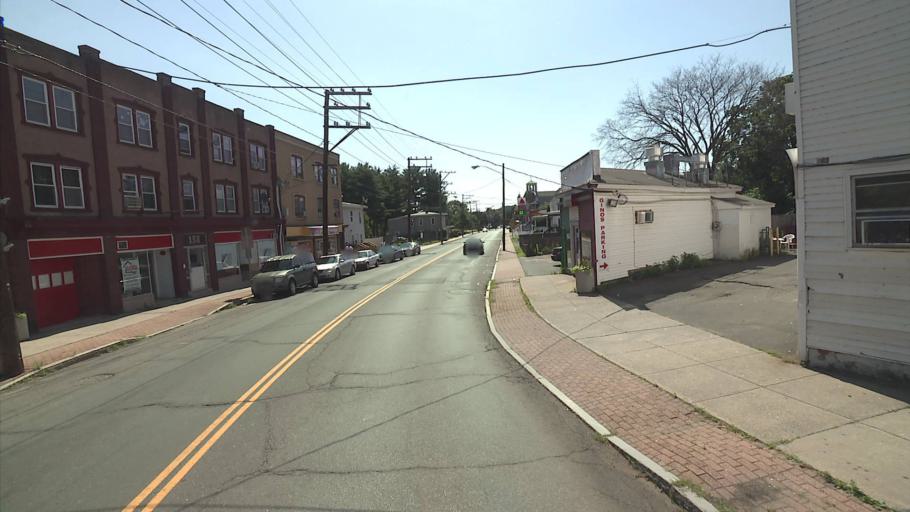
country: US
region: Connecticut
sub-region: Hartford County
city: Bristol
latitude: 41.6718
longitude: -72.9487
